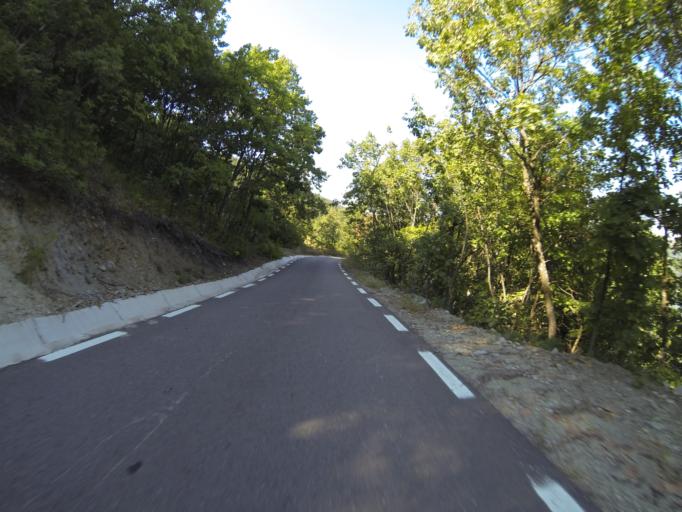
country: RO
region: Mehedinti
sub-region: Comuna Dubova
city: Dubova
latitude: 44.5349
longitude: 22.2050
